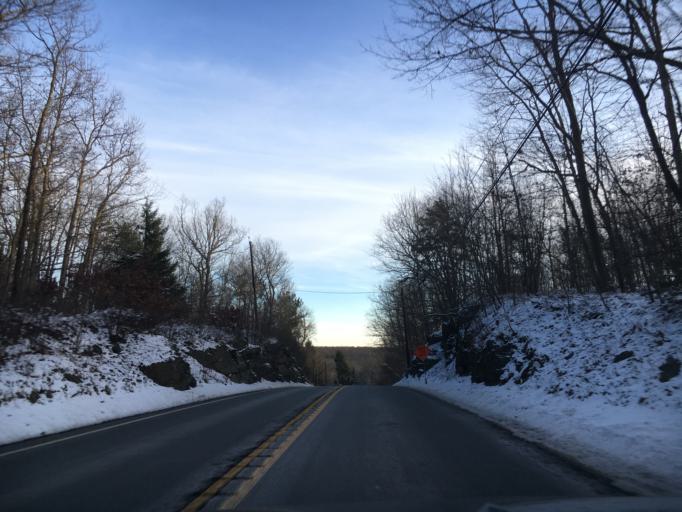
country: US
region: Pennsylvania
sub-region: Pike County
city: Hemlock Farms
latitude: 41.2819
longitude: -75.0911
